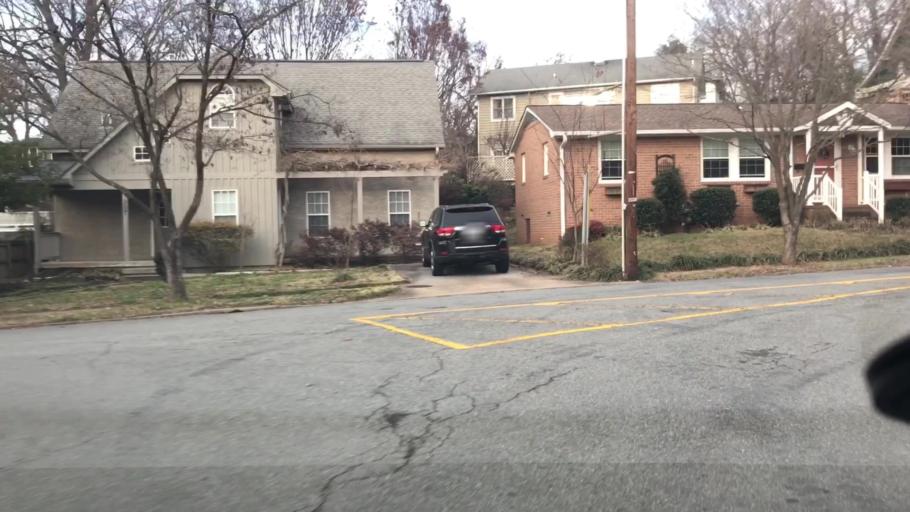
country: US
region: Virginia
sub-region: City of Charlottesville
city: Charlottesville
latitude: 38.0351
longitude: -78.4779
